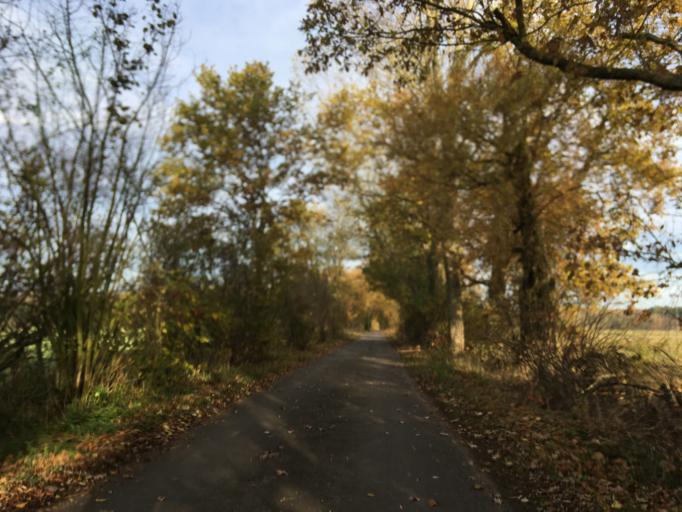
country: DE
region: Brandenburg
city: Luebben
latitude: 51.9822
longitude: 13.8732
